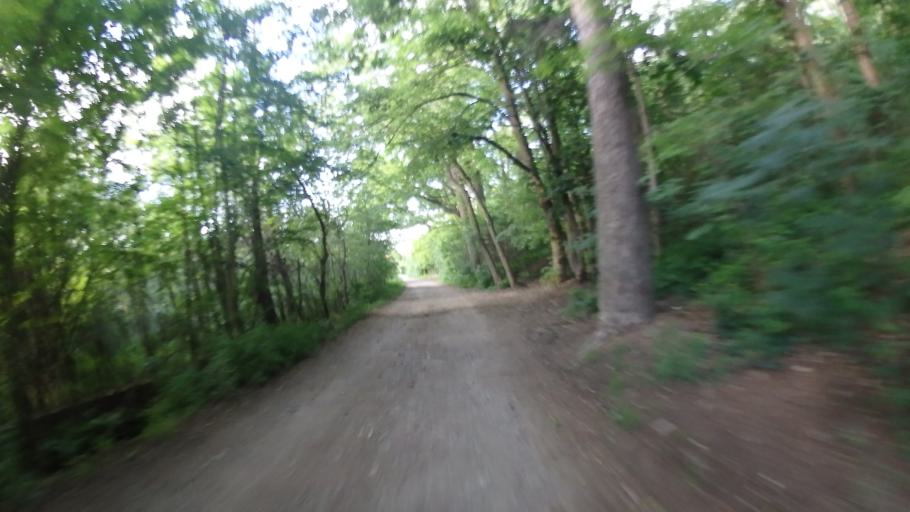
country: CZ
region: South Moravian
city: Ostopovice
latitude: 49.1613
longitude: 16.5381
